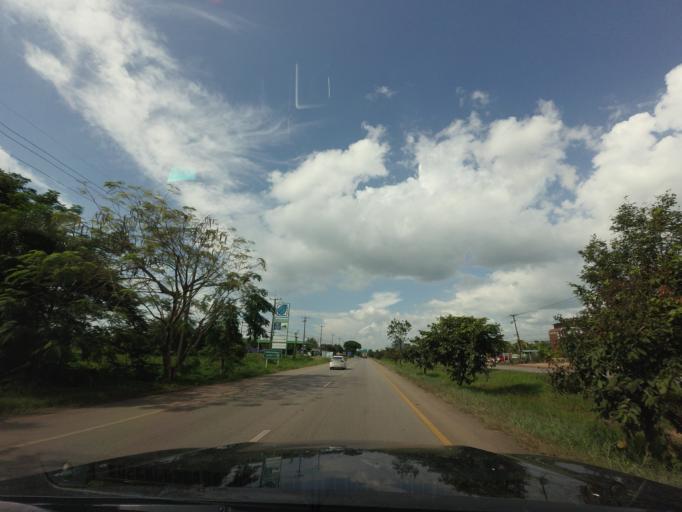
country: TH
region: Nong Khai
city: Sa Khrai
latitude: 17.5551
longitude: 102.8009
